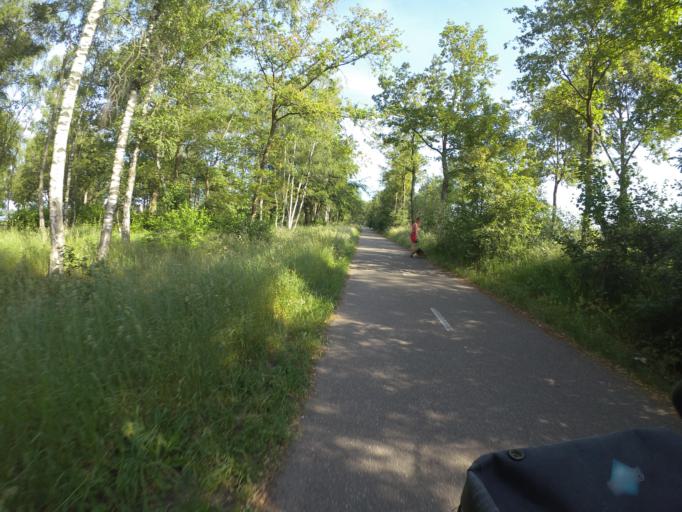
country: NL
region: Gelderland
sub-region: Gemeente Winterswijk
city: Winterswijk
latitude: 51.9925
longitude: 6.7261
